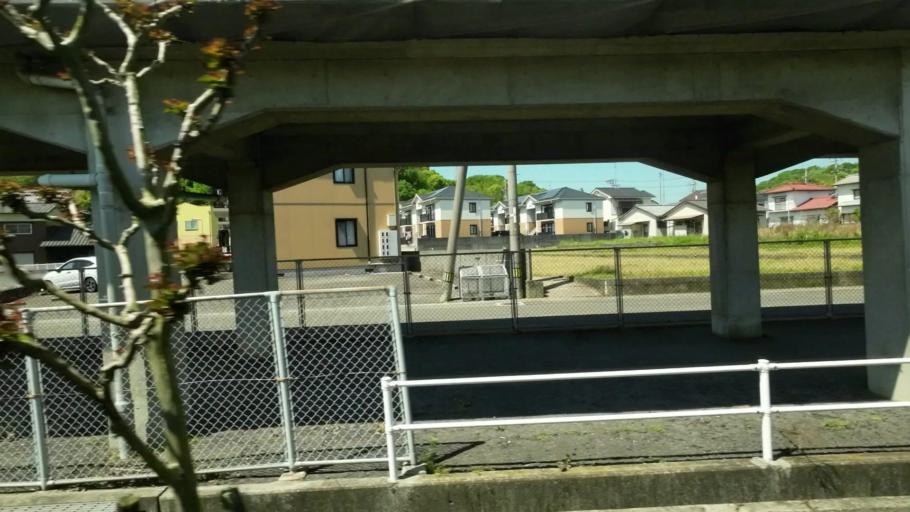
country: JP
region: Ehime
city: Hojo
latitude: 34.0722
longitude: 132.9870
